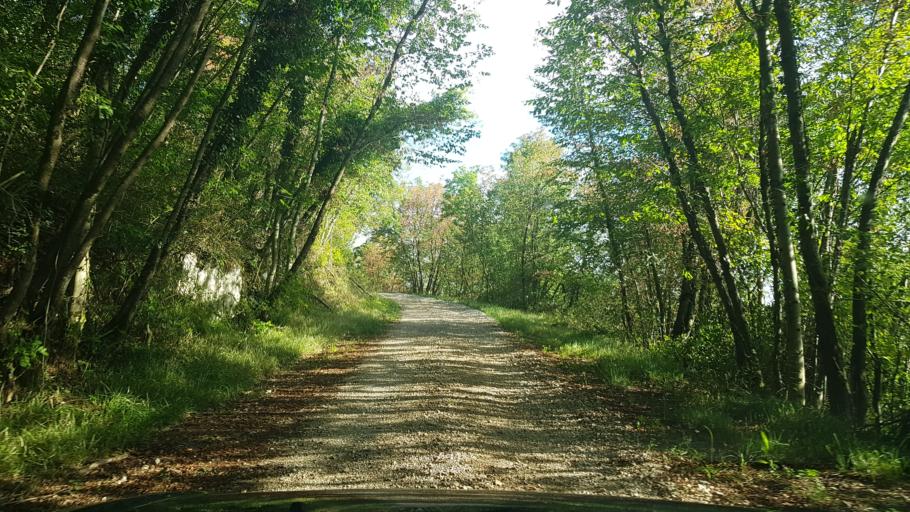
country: SI
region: Kanal
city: Deskle
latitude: 46.0180
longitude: 13.6195
